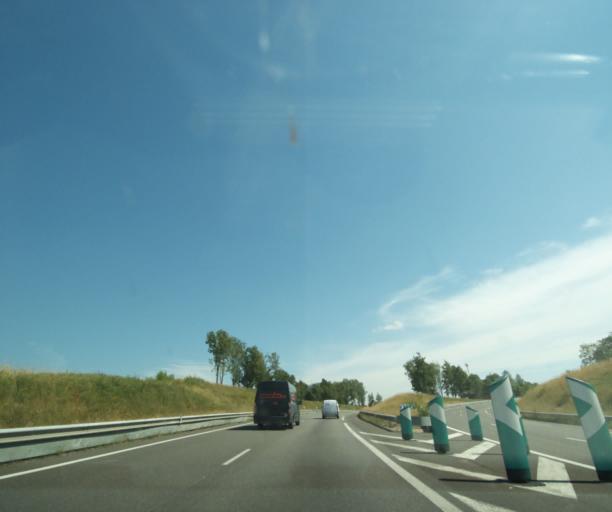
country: FR
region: Lorraine
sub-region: Departement de Meurthe-et-Moselle
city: Dommartin-les-Toul
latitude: 48.6503
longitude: 5.8807
